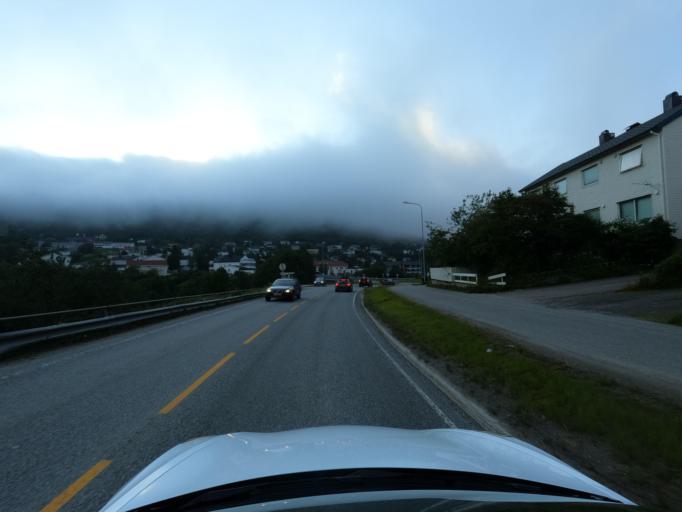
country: NO
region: Troms
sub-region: Harstad
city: Harstad
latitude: 68.8068
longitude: 16.5100
